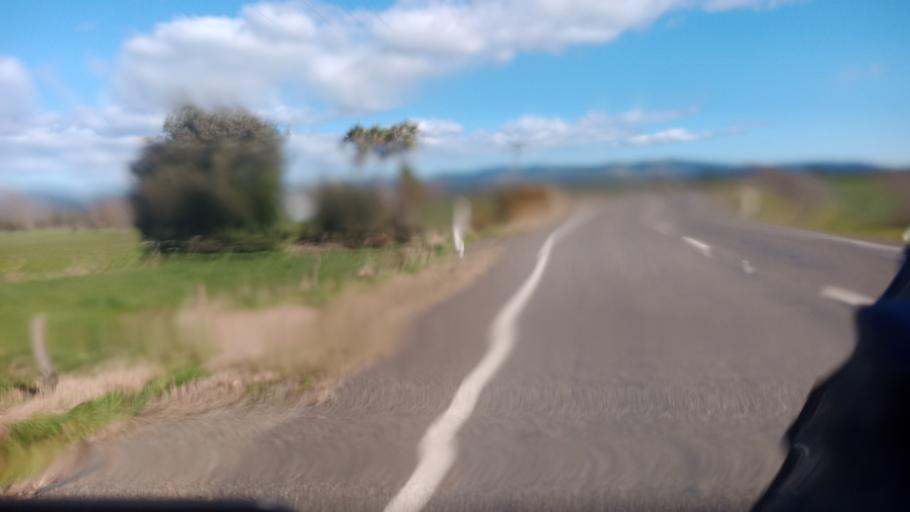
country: NZ
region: Bay of Plenty
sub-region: Opotiki District
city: Opotiki
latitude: -37.9936
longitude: 177.3041
